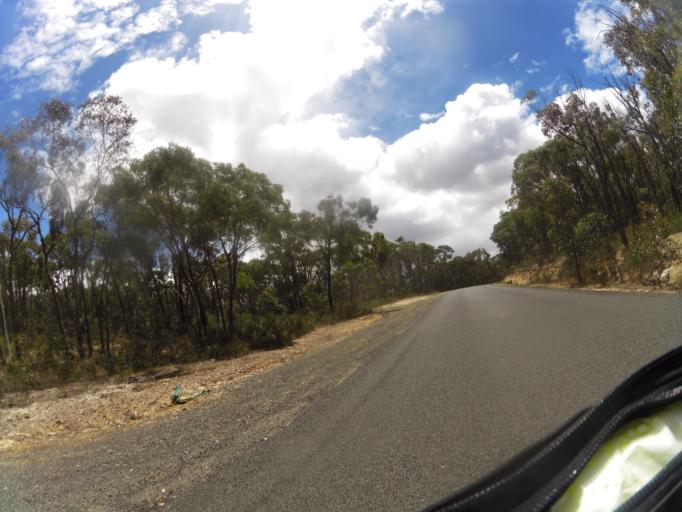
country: AU
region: Victoria
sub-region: Mount Alexander
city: Castlemaine
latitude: -37.0225
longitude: 144.2426
